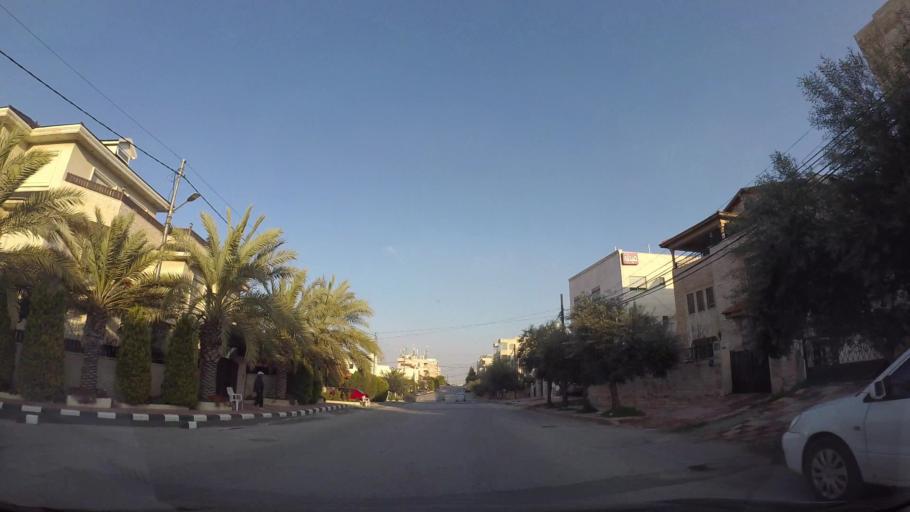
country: JO
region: Amman
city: Amman
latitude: 31.9862
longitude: 35.9592
